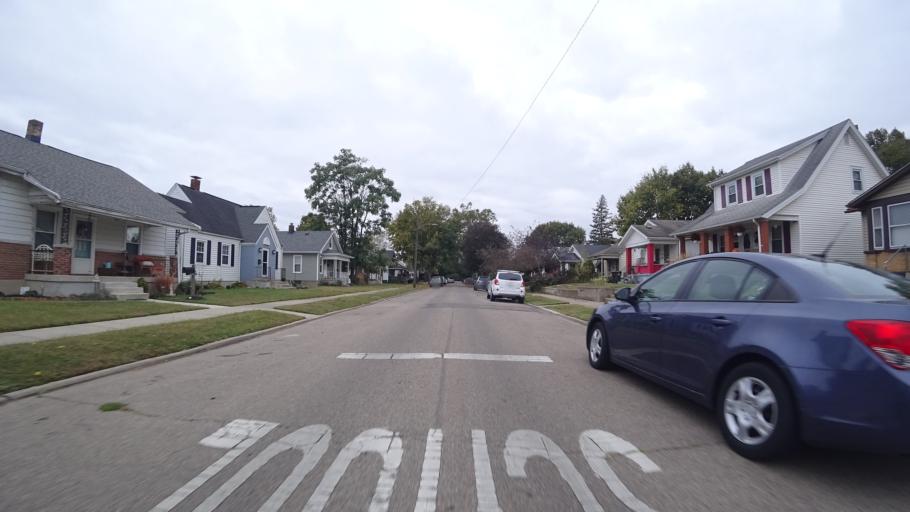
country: US
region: Ohio
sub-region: Butler County
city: Fairfield
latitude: 39.3671
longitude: -84.5614
